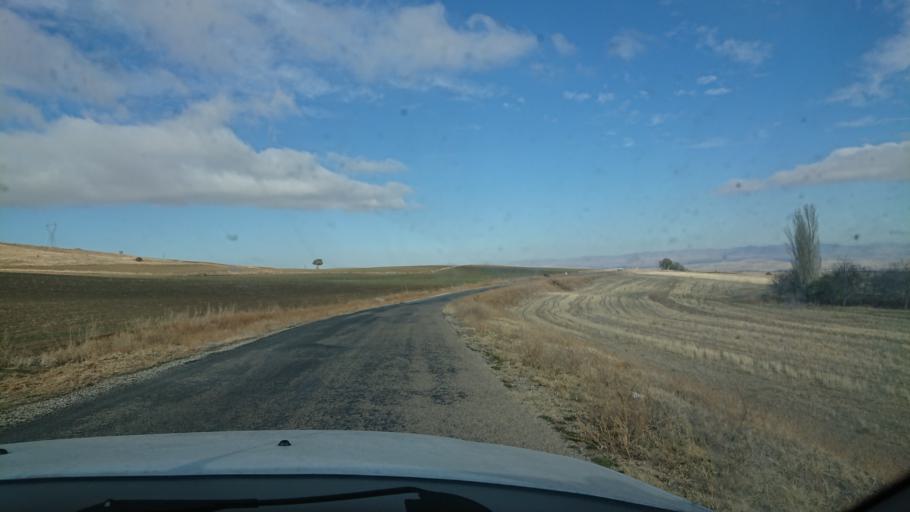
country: TR
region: Aksaray
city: Agacoren
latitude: 38.8446
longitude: 33.9497
